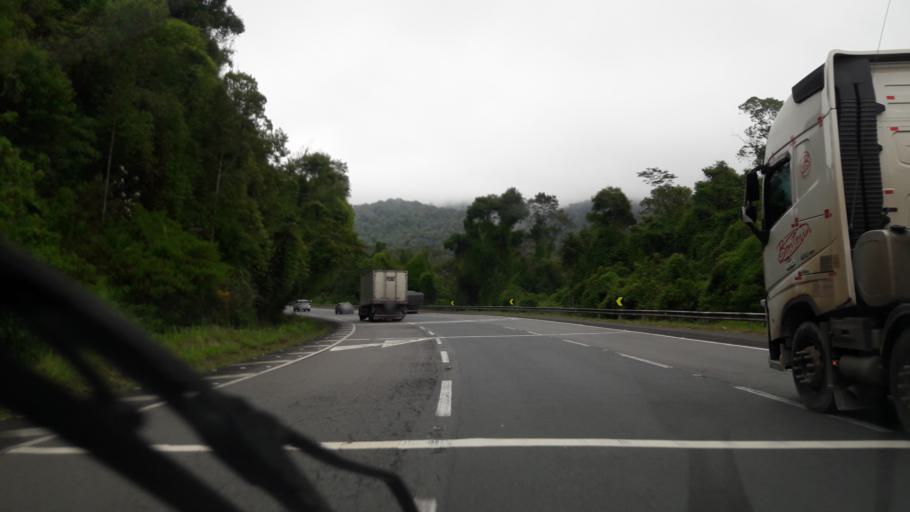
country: BR
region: Parana
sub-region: Antonina
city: Antonina
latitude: -25.0832
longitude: -48.6353
